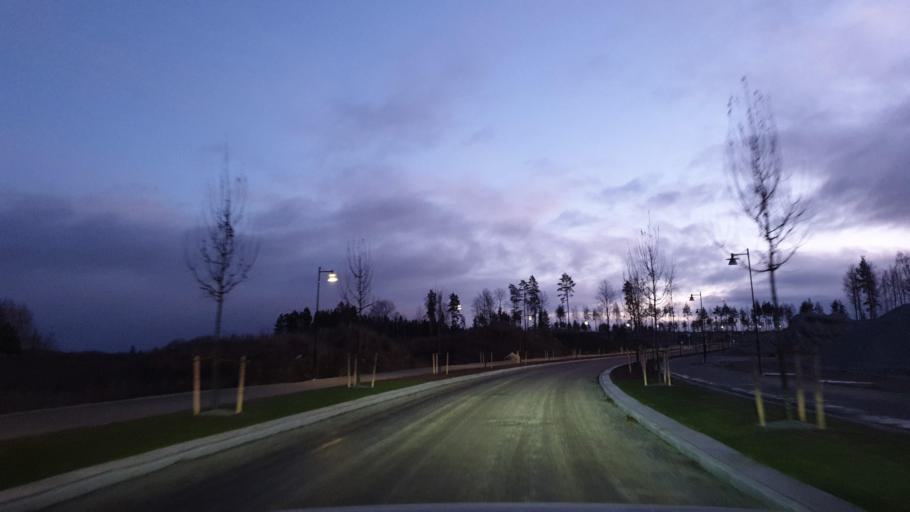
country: SE
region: Stockholm
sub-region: Sigtuna Kommun
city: Marsta
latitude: 59.6151
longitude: 17.7956
